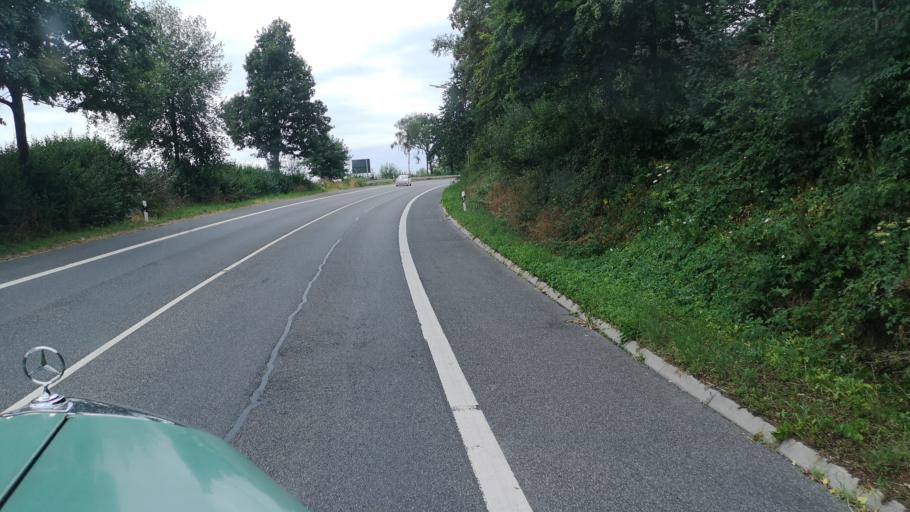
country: DE
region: North Rhine-Westphalia
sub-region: Regierungsbezirk Koln
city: Kurten
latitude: 51.0550
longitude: 7.2346
